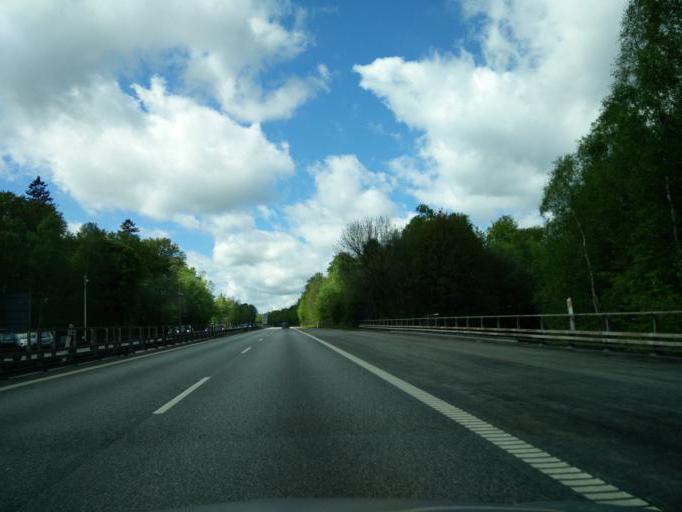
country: DK
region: Capital Region
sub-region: Herlev Kommune
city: Herlev
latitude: 55.7673
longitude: 12.4294
